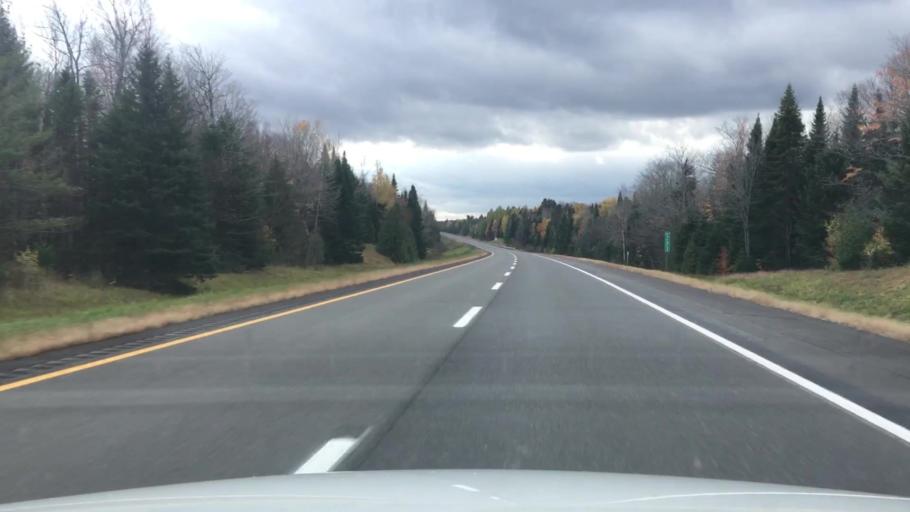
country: US
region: Maine
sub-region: Penobscot County
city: Patten
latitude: 46.0879
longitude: -68.2063
